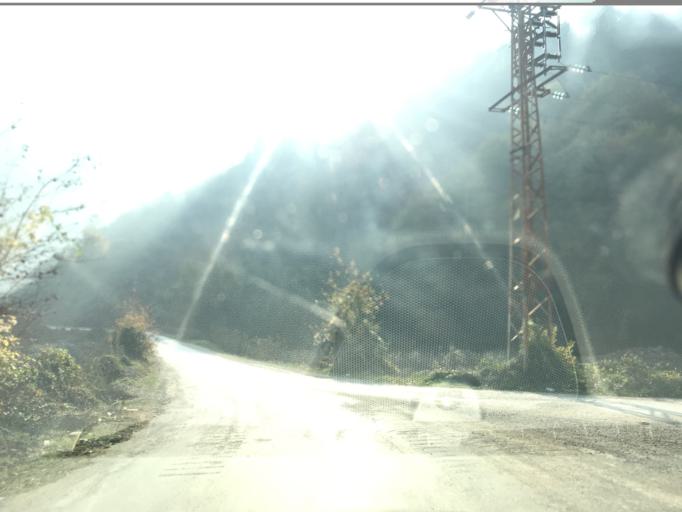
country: TR
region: Duzce
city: Cumayeri
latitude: 40.9295
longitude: 30.9257
